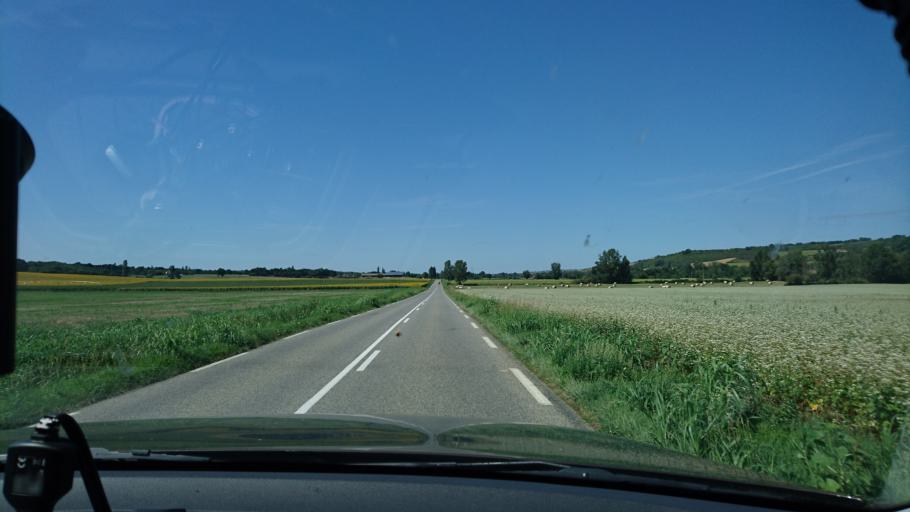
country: FR
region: Midi-Pyrenees
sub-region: Departement de l'Ariege
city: Lezat-sur-Leze
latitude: 43.2481
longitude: 1.3651
